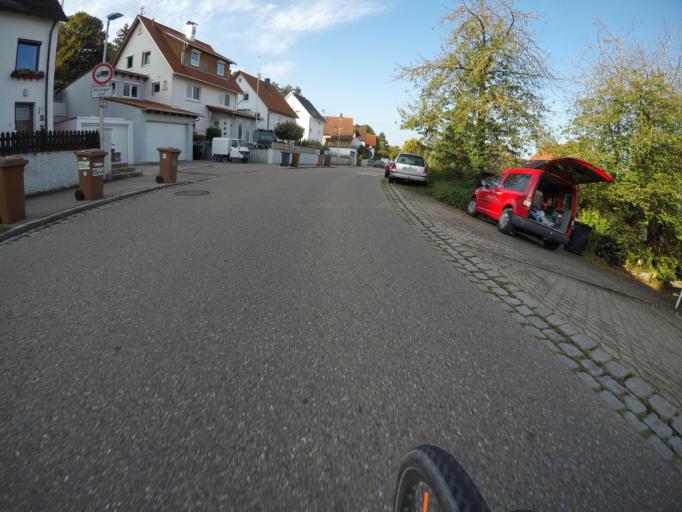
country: DE
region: Baden-Wuerttemberg
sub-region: Regierungsbezirk Stuttgart
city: Herbrechtingen
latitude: 48.6223
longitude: 10.1638
